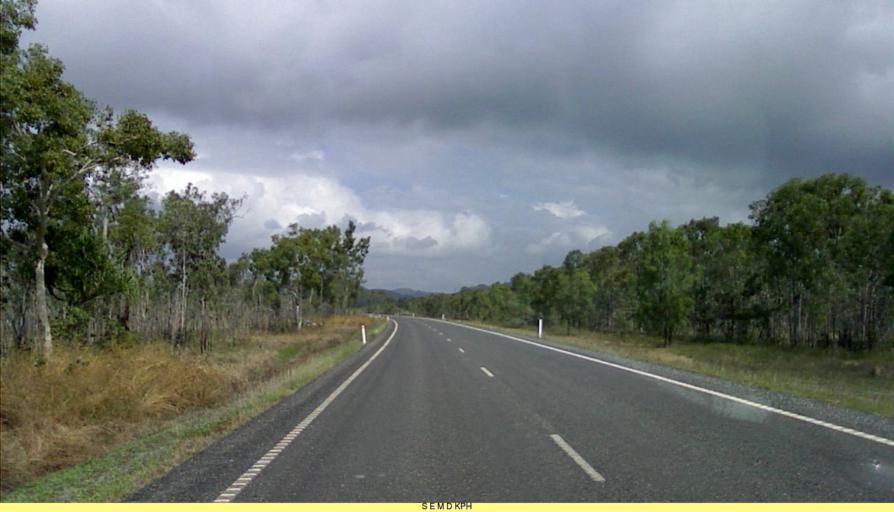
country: AU
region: Queensland
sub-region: Cook
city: Cooktown
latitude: -15.7306
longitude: 145.0225
